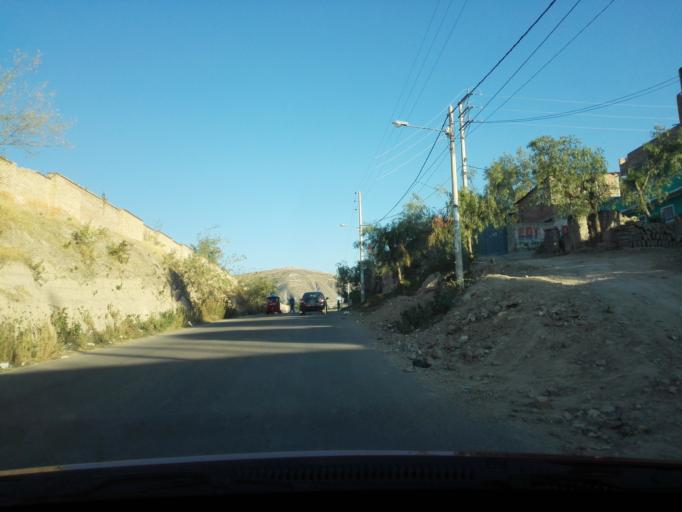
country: PE
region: Ayacucho
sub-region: Provincia de Huamanga
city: Ayacucho
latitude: -13.1456
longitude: -74.2174
